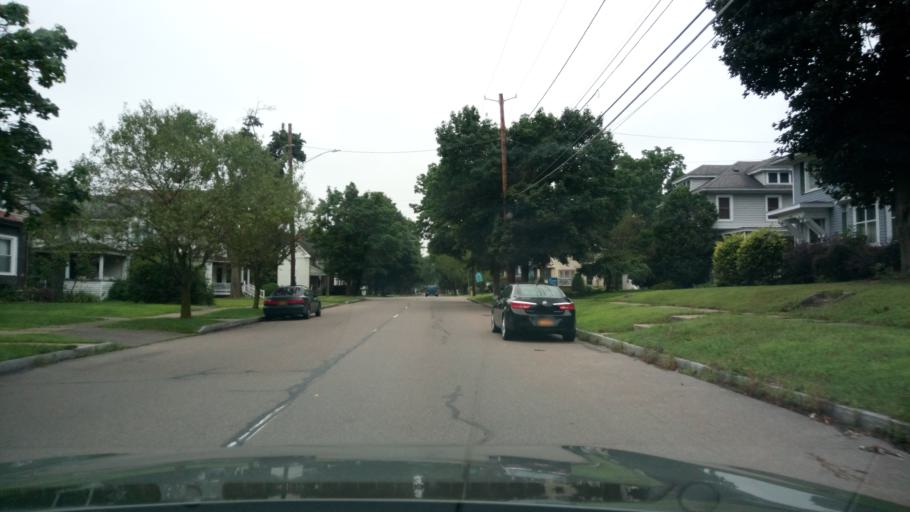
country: US
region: New York
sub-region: Chemung County
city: Elmira
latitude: 42.0849
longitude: -76.8252
